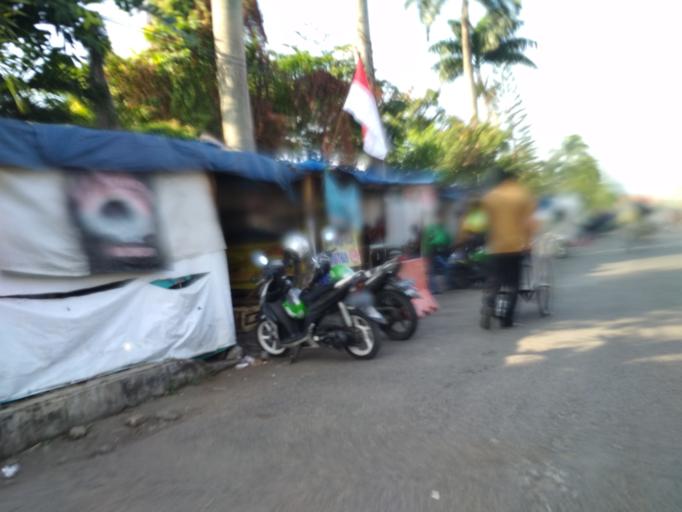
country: ID
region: West Java
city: Bogor
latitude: -6.5924
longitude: 106.7903
